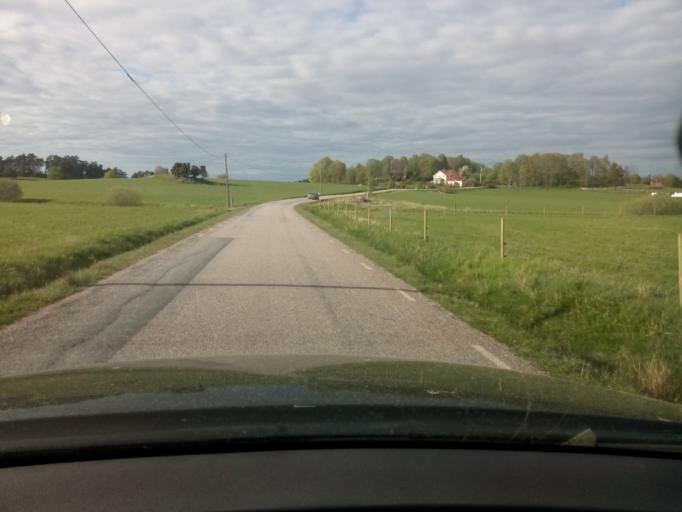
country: SE
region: Soedermanland
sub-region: Nykopings Kommun
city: Stigtomta
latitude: 58.9186
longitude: 16.8789
